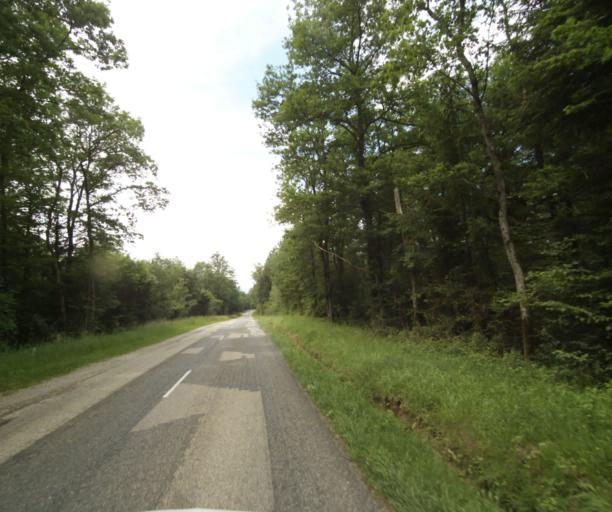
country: FR
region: Rhone-Alpes
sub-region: Departement de la Haute-Savoie
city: Sciez
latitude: 46.3127
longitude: 6.4030
